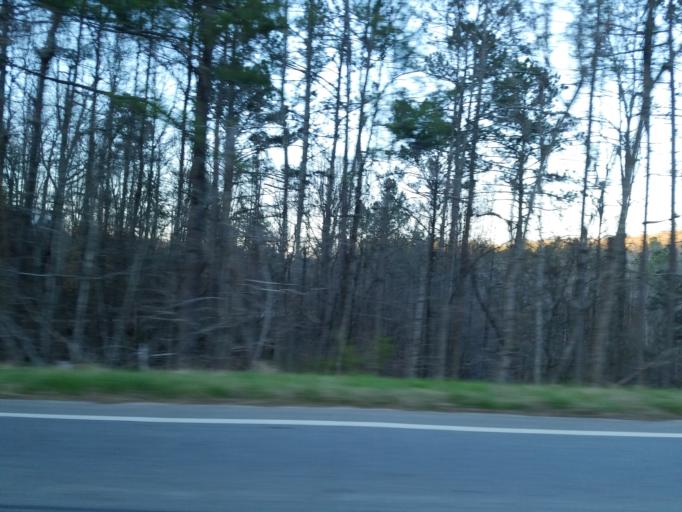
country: US
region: Georgia
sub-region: Dawson County
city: Dawsonville
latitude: 34.3325
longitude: -84.0150
